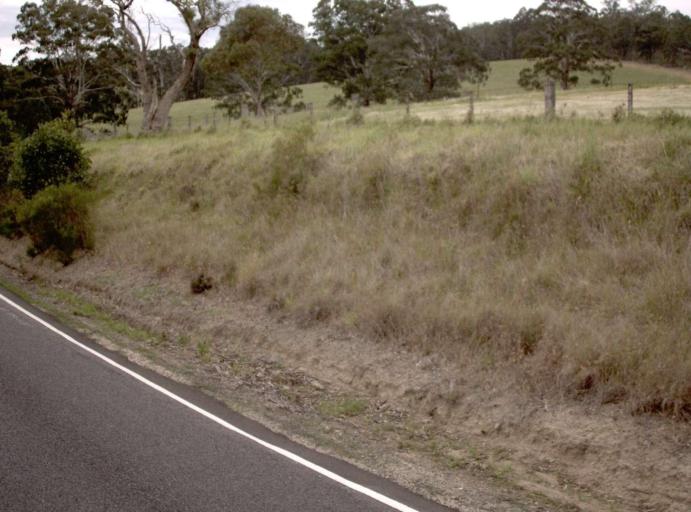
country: AU
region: New South Wales
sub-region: Bombala
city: Bombala
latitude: -37.4830
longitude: 149.1801
